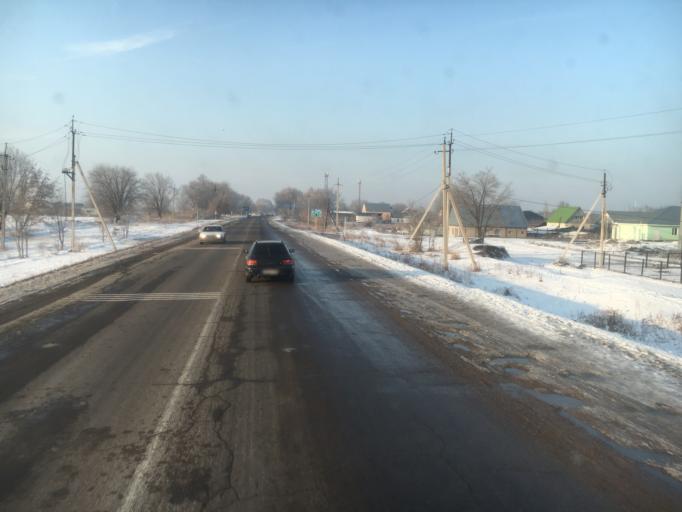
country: KZ
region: Almaty Oblysy
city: Burunday
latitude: 43.3328
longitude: 76.6615
